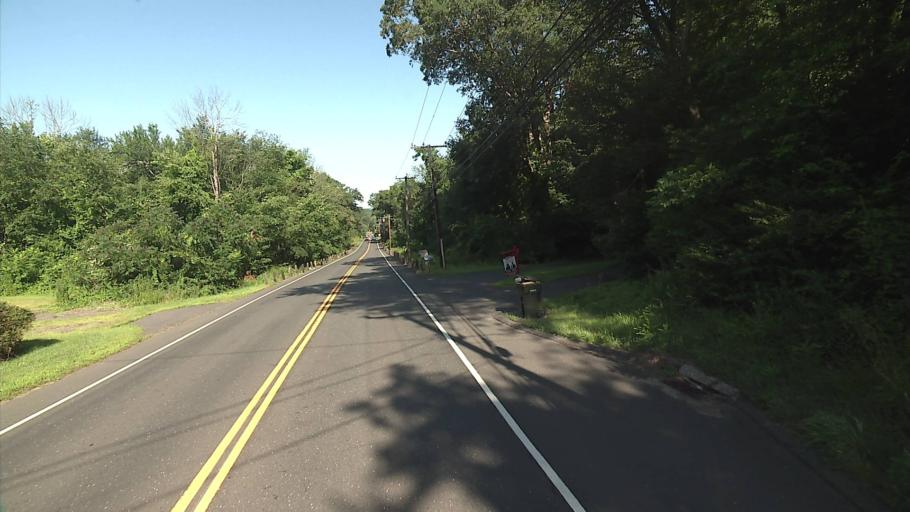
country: US
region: Connecticut
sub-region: Hartford County
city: Tariffville
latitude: 41.9503
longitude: -72.7537
